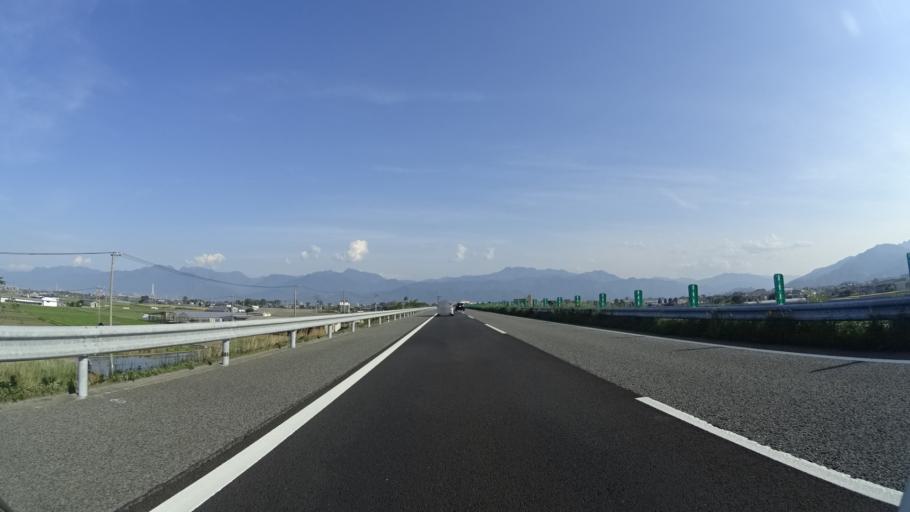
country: JP
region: Ehime
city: Saijo
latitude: 33.9580
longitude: 133.0660
